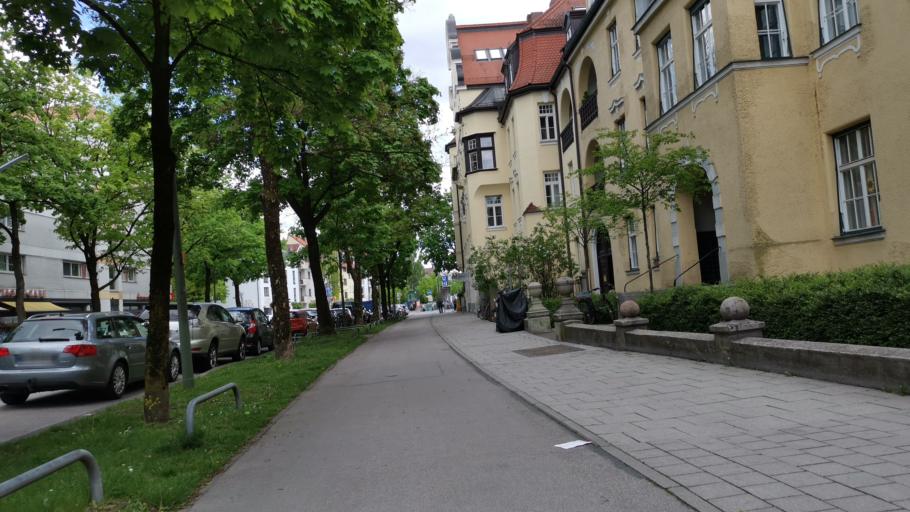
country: DE
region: Bavaria
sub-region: Upper Bavaria
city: Munich
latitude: 48.1647
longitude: 11.5284
